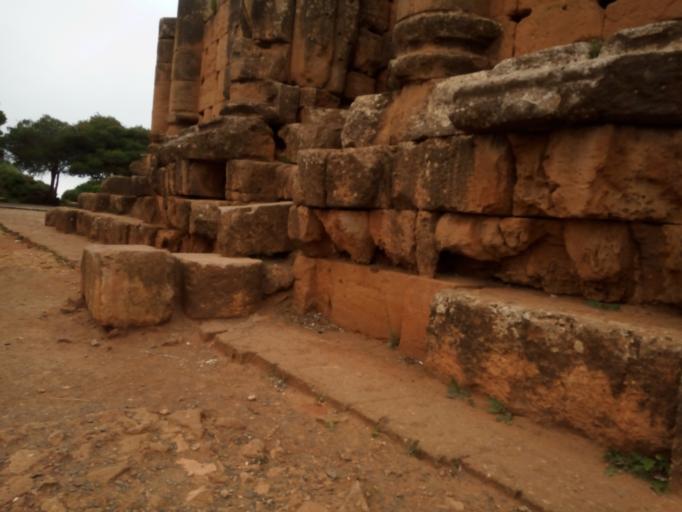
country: DZ
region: Tipaza
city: Tipasa
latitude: 36.5747
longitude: 2.5529
